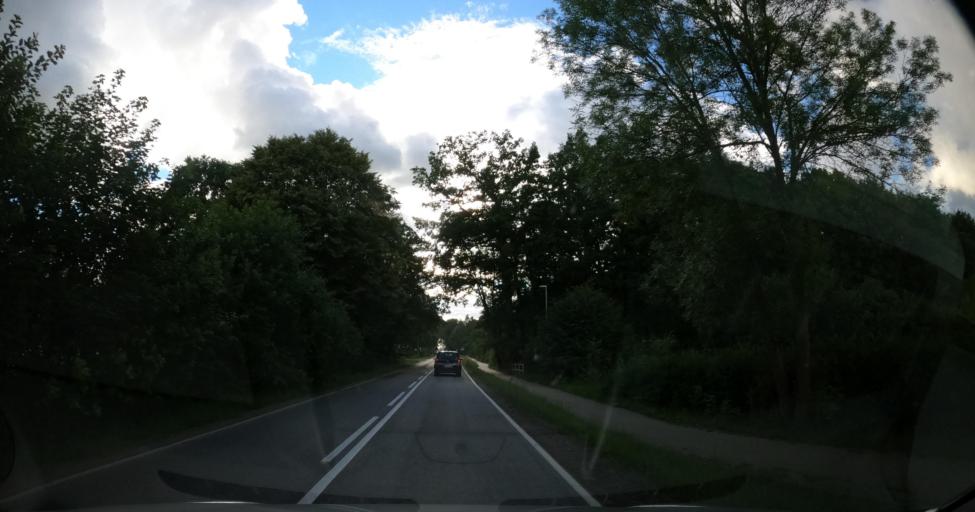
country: PL
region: Pomeranian Voivodeship
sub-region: Powiat slupski
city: Potegowo
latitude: 54.4190
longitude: 17.3923
